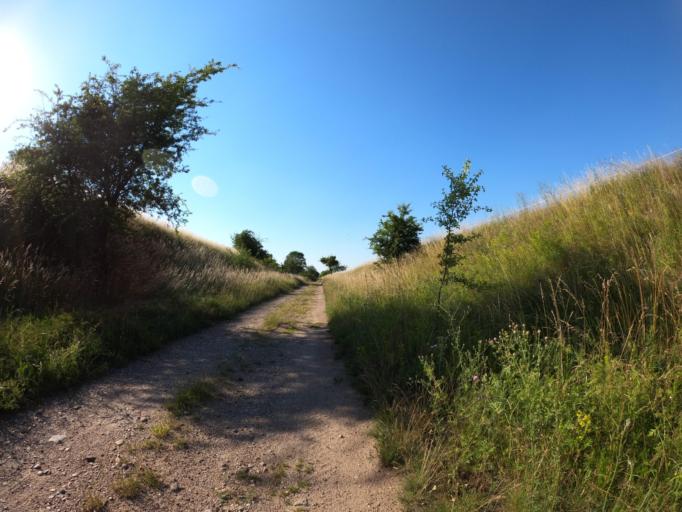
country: DE
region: Brandenburg
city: Gartz
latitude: 53.2190
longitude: 14.3745
